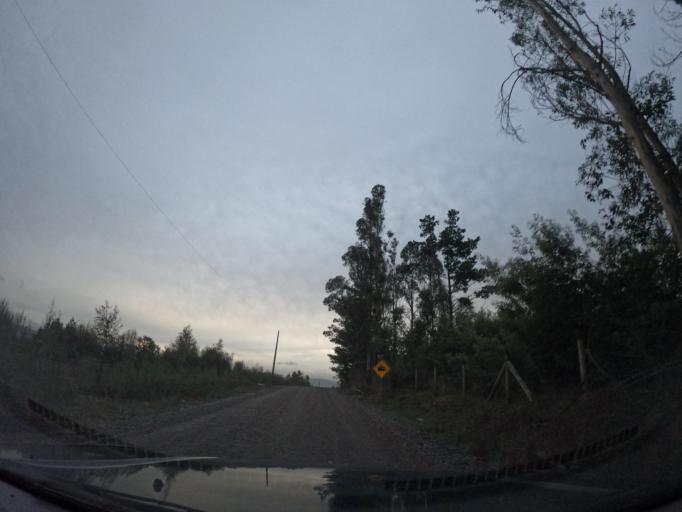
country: CL
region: Biobio
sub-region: Provincia de Concepcion
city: Chiguayante
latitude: -37.0126
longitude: -72.8652
